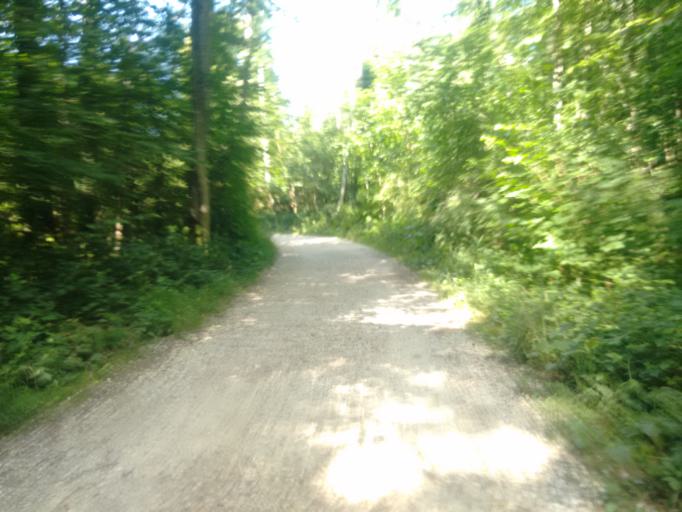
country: AT
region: Upper Austria
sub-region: Wels-Land
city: Thalheim bei Wels
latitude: 48.1437
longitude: 14.0116
